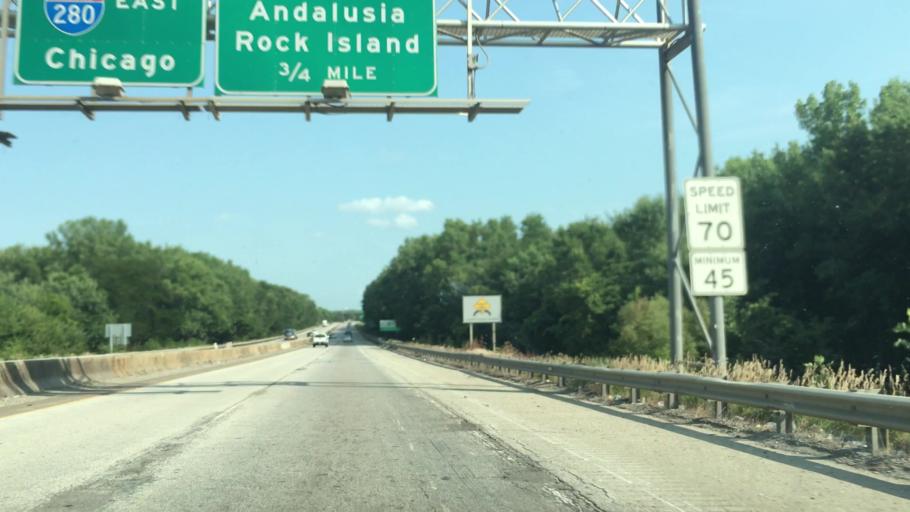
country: US
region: Illinois
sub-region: Rock Island County
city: Milan
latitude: 41.4744
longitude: -90.6264
